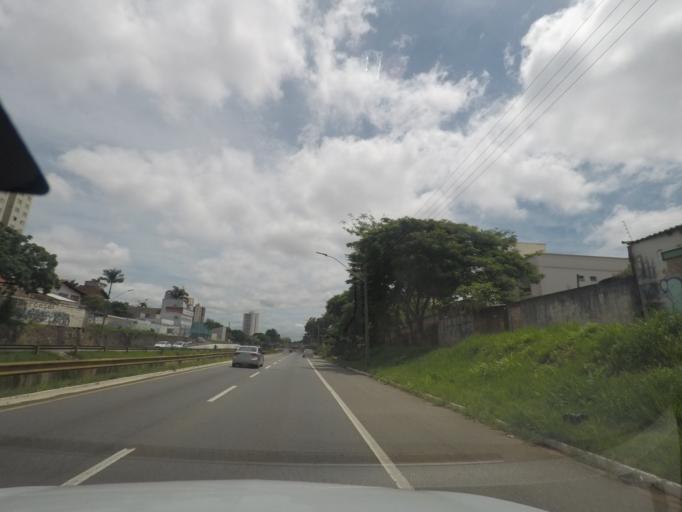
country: BR
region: Goias
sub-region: Goiania
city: Goiania
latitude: -16.6779
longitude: -49.2494
